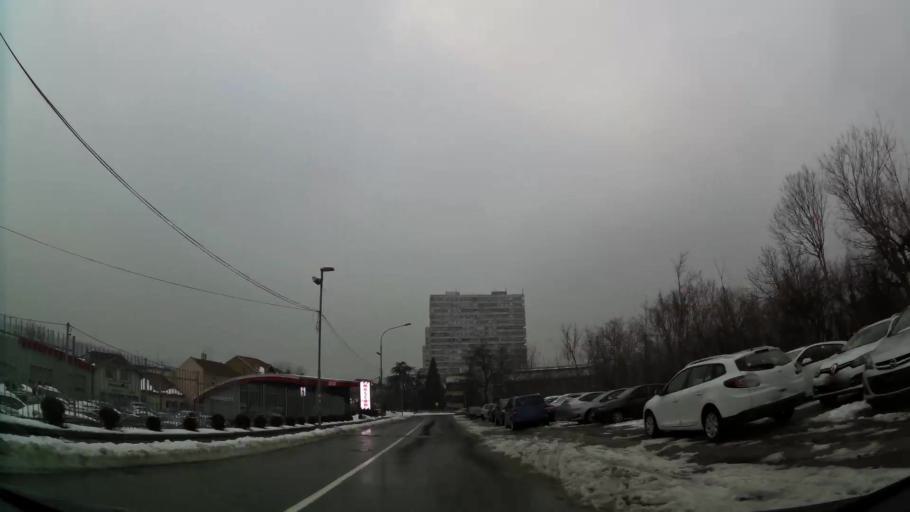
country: RS
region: Central Serbia
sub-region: Belgrade
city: Vozdovac
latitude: 44.7823
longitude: 20.4923
